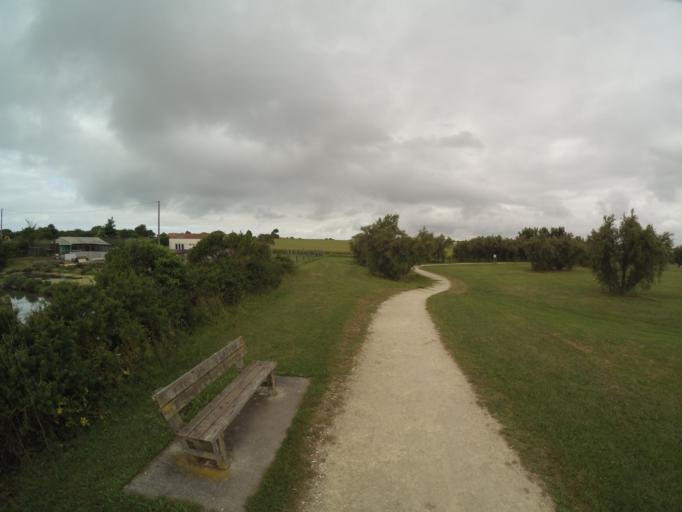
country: FR
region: Poitou-Charentes
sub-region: Departement de la Charente-Maritime
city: Aytre
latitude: 46.1300
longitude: -1.1312
